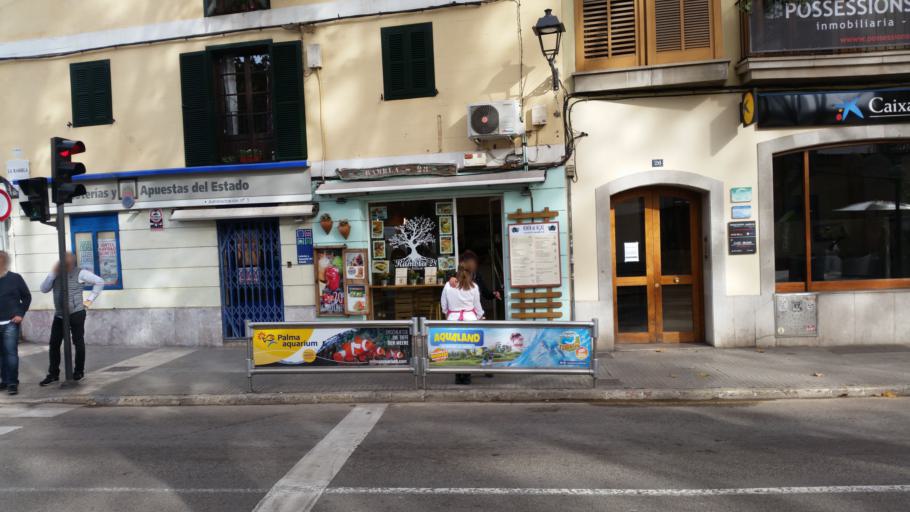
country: ES
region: Balearic Islands
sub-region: Illes Balears
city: Palma
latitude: 39.5747
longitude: 2.6484
